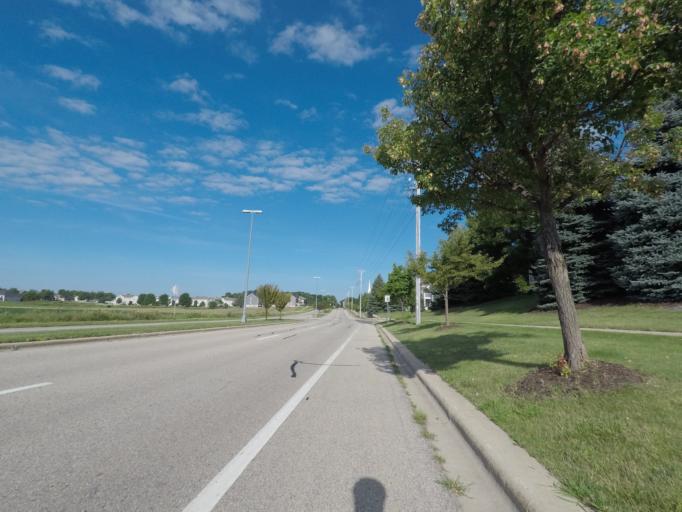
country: US
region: Wisconsin
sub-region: Dane County
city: Middleton
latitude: 43.0749
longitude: -89.5446
